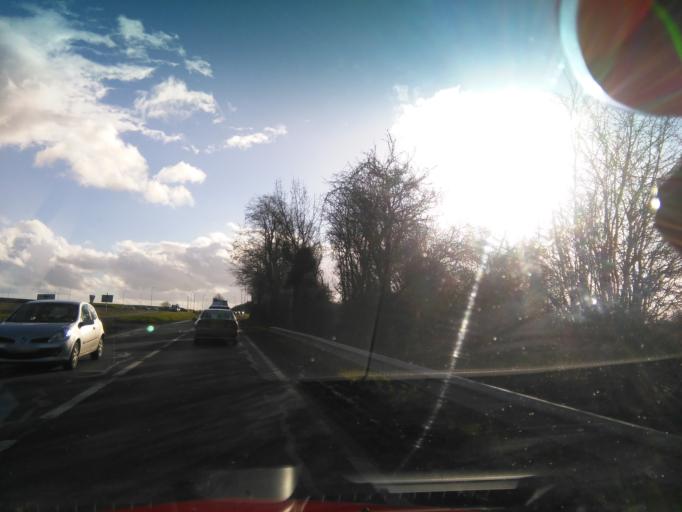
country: FR
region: Lower Normandy
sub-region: Departement du Calvados
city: Bretteville-sur-Odon
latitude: 49.1555
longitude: -0.4144
